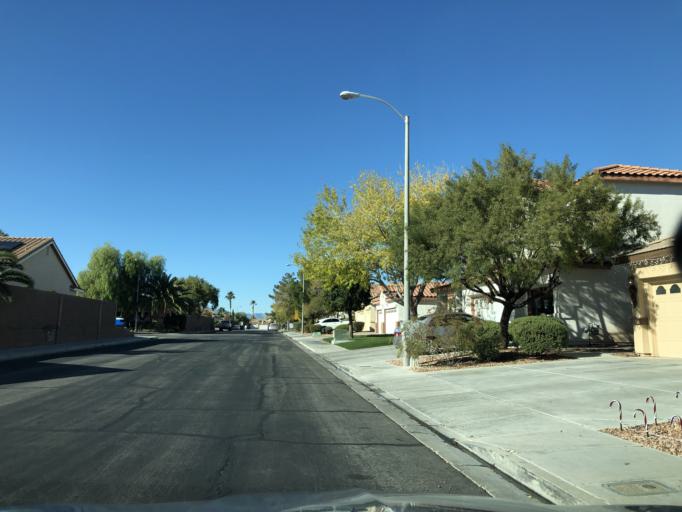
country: US
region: Nevada
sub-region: Clark County
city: Whitney
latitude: 36.0110
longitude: -115.0854
